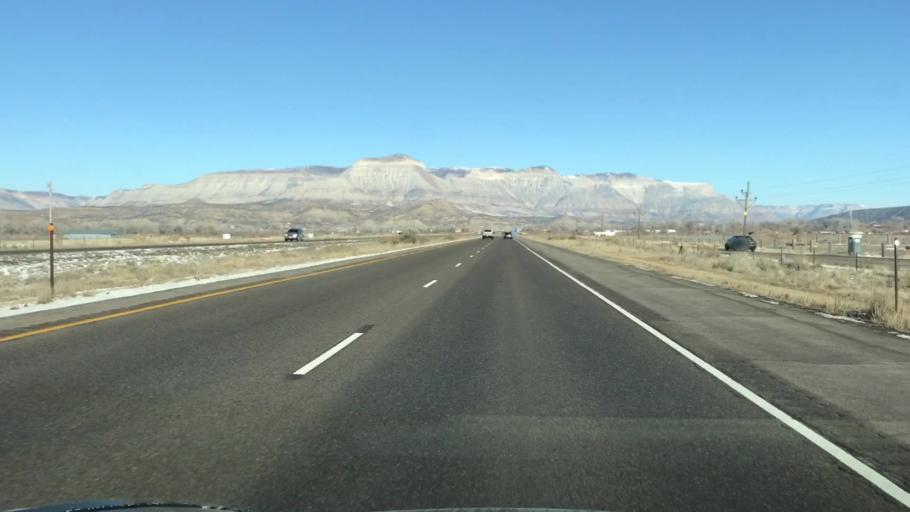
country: US
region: Colorado
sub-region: Garfield County
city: Parachute
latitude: 39.2986
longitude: -108.2202
